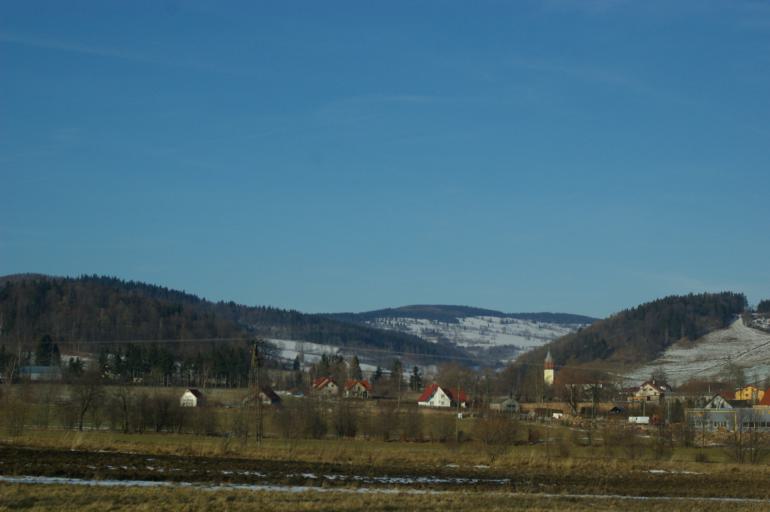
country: PL
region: Lower Silesian Voivodeship
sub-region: Powiat kamiennogorski
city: Kamienna Gora
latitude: 50.7772
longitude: 15.9552
